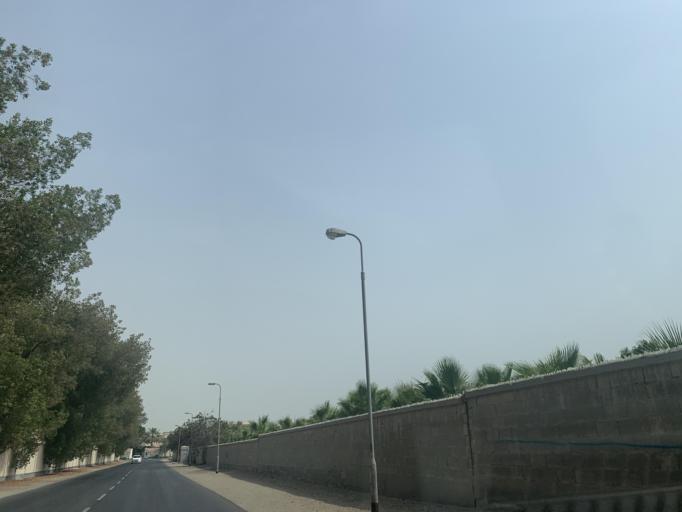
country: BH
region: Manama
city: Jidd Hafs
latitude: 26.2028
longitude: 50.4721
